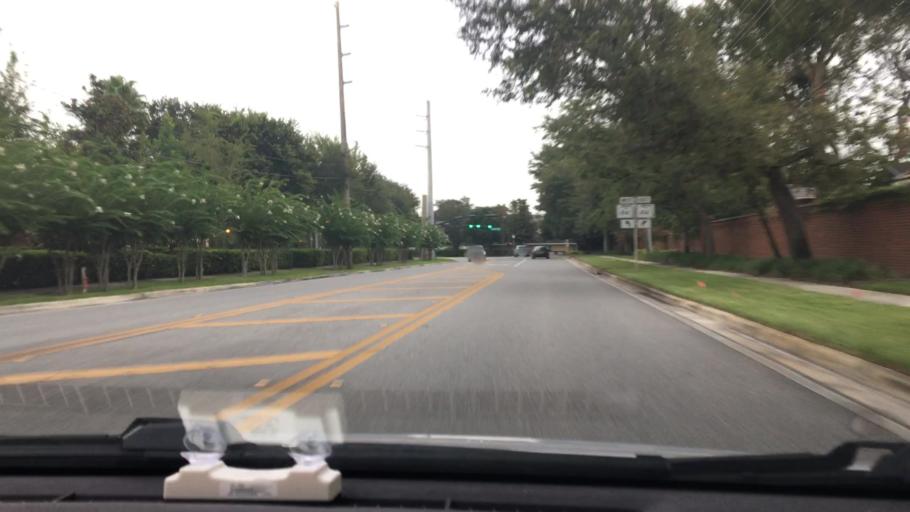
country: US
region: Florida
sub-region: Orange County
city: Eatonville
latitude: 28.6281
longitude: -81.3858
